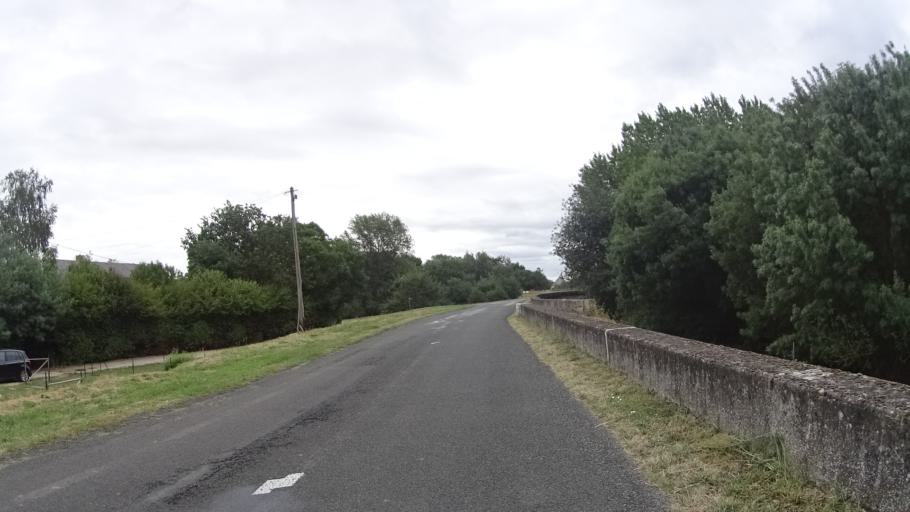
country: FR
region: Pays de la Loire
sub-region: Departement de Maine-et-Loire
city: Chalonnes-sur-Loire
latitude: 47.3658
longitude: -0.7322
